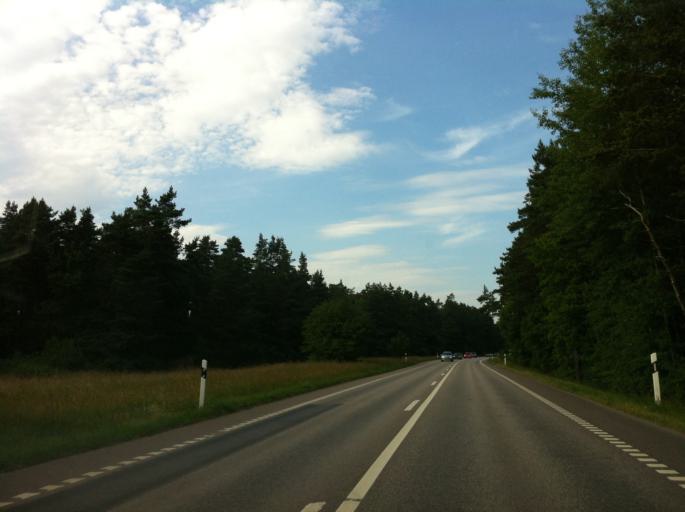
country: SE
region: Kalmar
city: Faerjestaden
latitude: 56.7477
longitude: 16.5483
